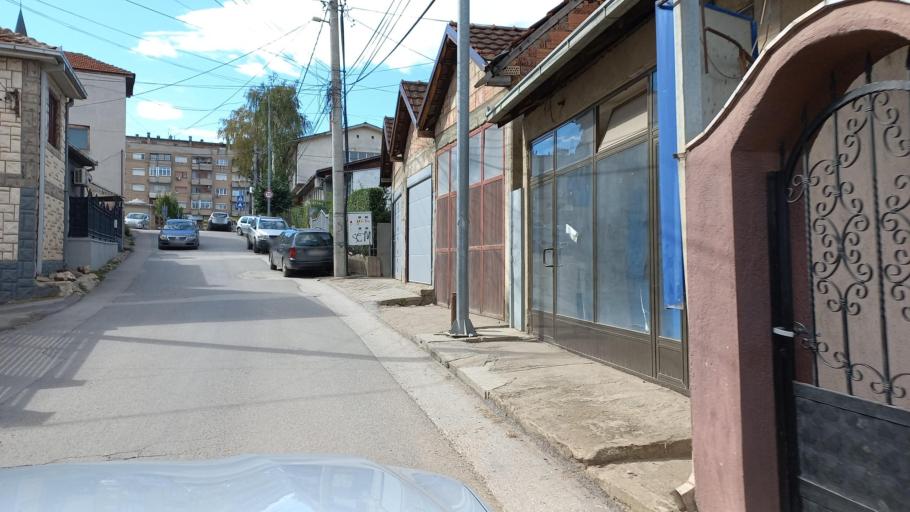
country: MK
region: Kumanovo
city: Kumanovo
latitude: 42.1384
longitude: 21.7146
